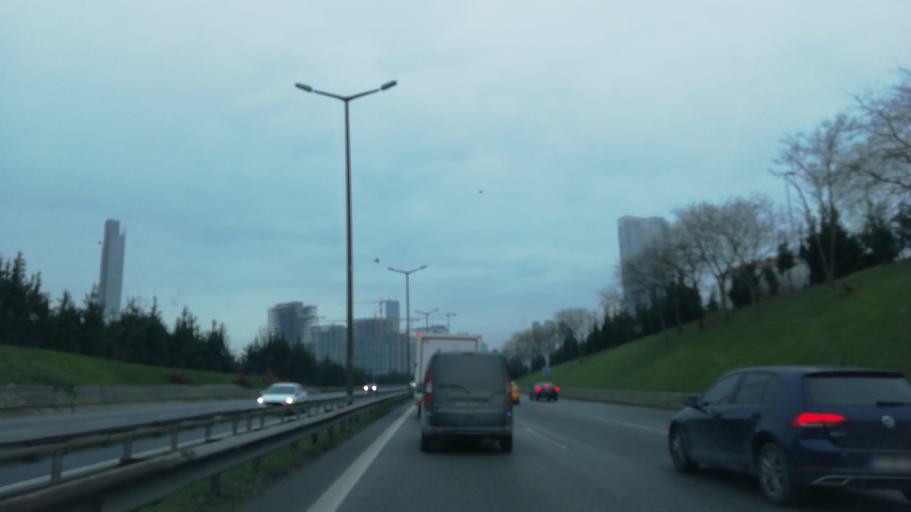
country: TR
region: Istanbul
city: Umraniye
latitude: 41.0070
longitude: 29.0976
